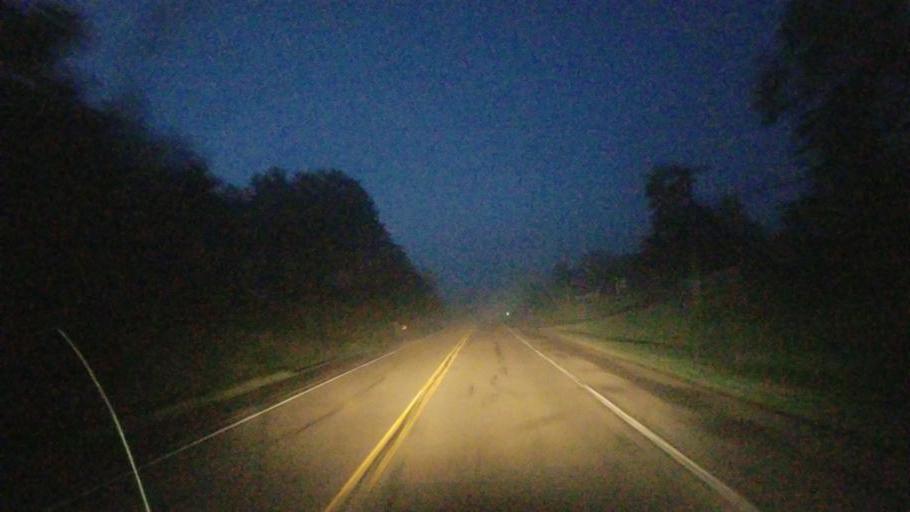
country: US
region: New York
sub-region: Allegany County
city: Wellsville
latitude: 42.0416
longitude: -77.9153
